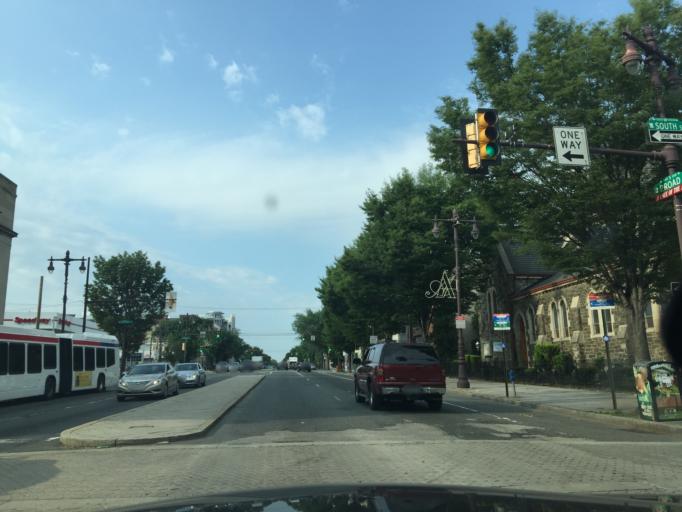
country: US
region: Pennsylvania
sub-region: Philadelphia County
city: Philadelphia
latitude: 39.9437
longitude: -75.1656
